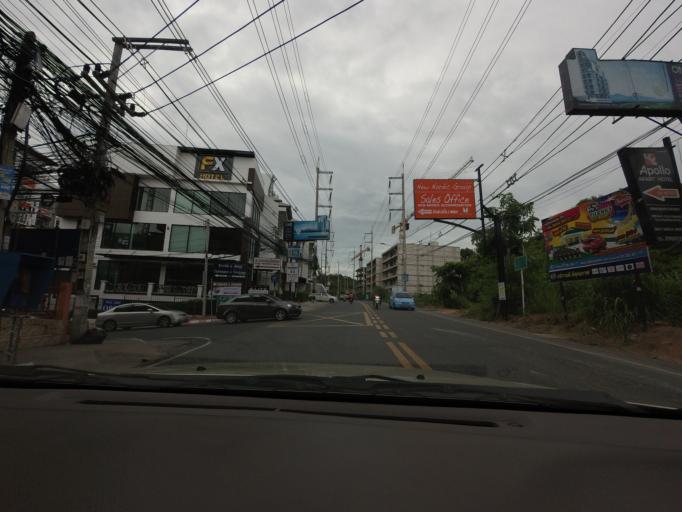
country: TH
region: Chon Buri
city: Phatthaya
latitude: 12.9156
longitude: 100.8669
